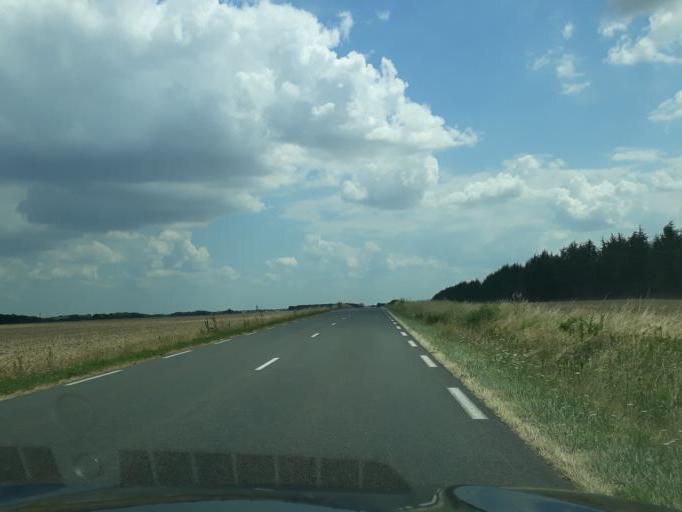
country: FR
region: Centre
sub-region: Departement du Cher
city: Avord
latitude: 47.0379
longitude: 2.5983
